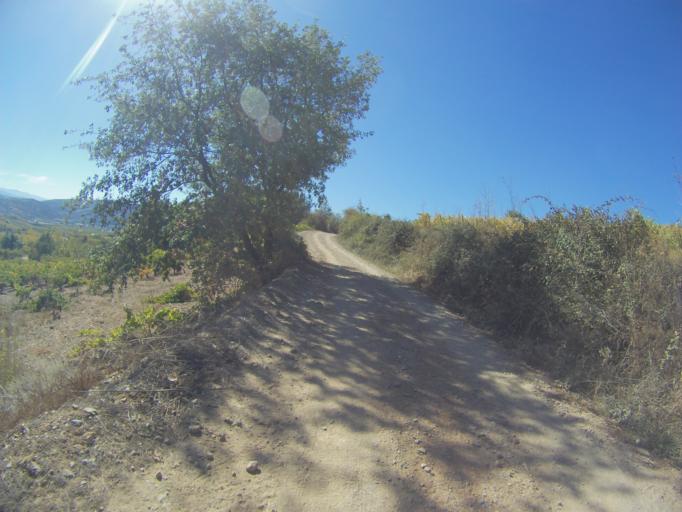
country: ES
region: Castille and Leon
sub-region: Provincia de Leon
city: Villafranca del Bierzo
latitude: 42.6050
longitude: -6.7852
